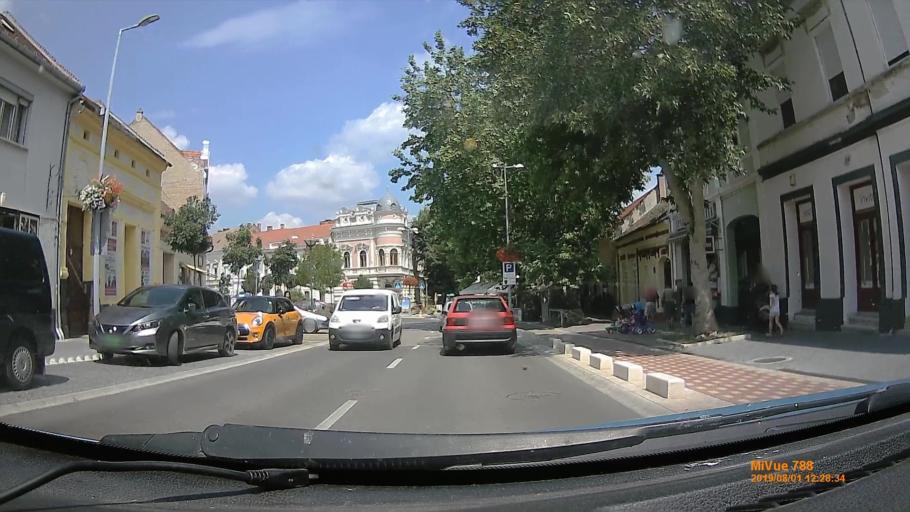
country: HU
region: Baranya
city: Siklos
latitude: 45.8534
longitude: 18.2983
